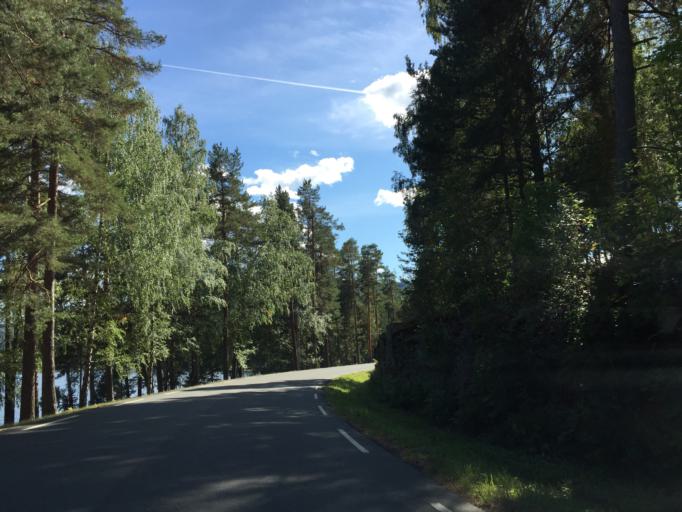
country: NO
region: Buskerud
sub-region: Ovre Eiker
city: Hokksund
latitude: 59.6984
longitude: 9.8442
